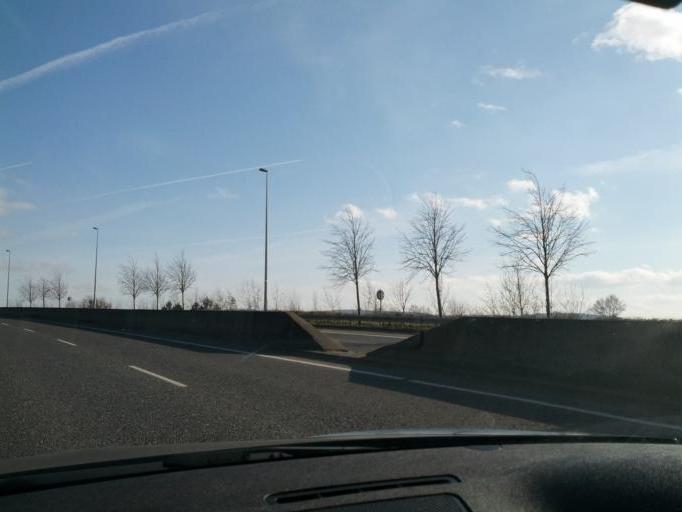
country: IE
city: Jobstown
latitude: 53.3052
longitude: -6.4234
